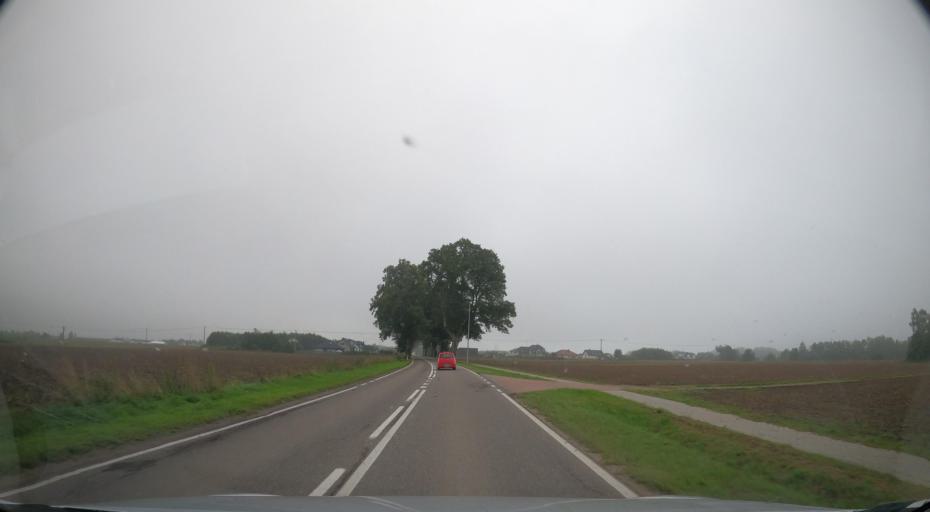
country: PL
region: Pomeranian Voivodeship
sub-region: Powiat wejherowski
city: Bojano
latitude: 54.4499
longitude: 18.3758
